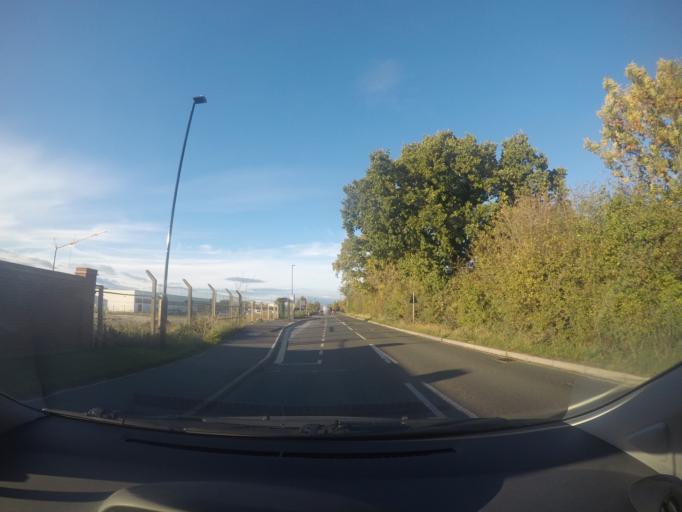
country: GB
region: England
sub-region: City of York
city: York
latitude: 53.9832
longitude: -1.0942
